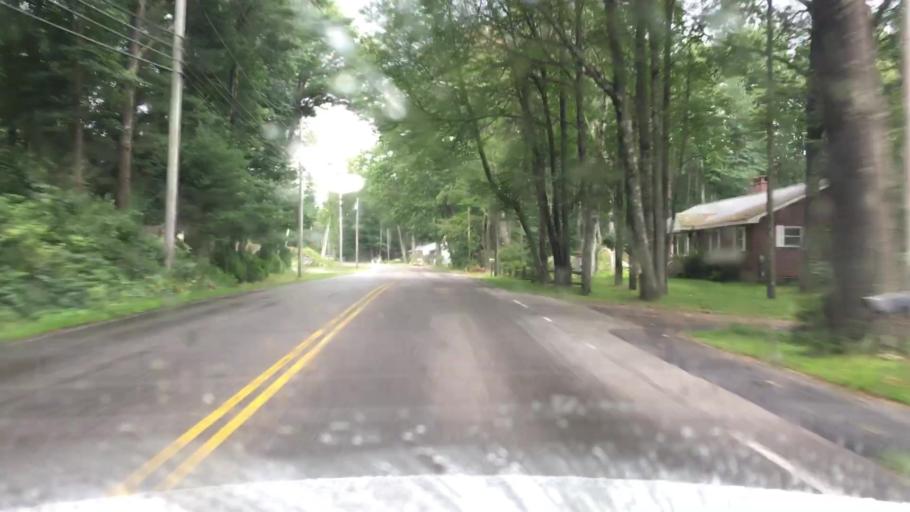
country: US
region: Maine
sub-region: York County
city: Wells Beach Station
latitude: 43.2954
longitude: -70.5941
